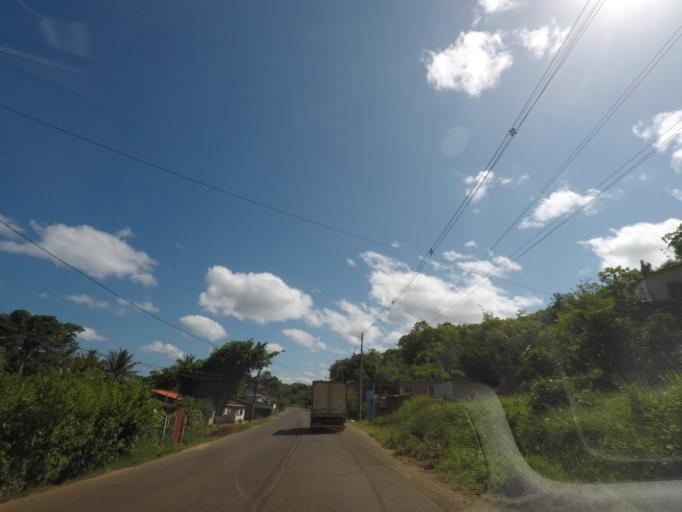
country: BR
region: Bahia
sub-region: Itubera
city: Itubera
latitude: -13.7541
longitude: -39.1543
